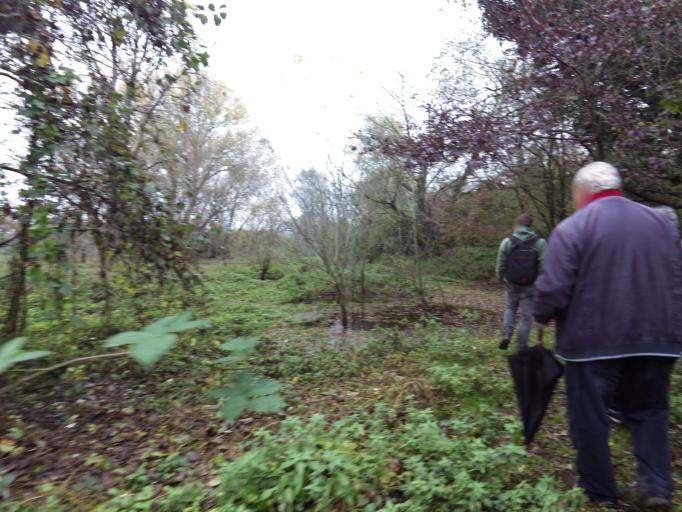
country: IT
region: Lombardy
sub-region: Citta metropolitana di Milano
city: San Donato Milanese
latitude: 45.4254
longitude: 9.2832
